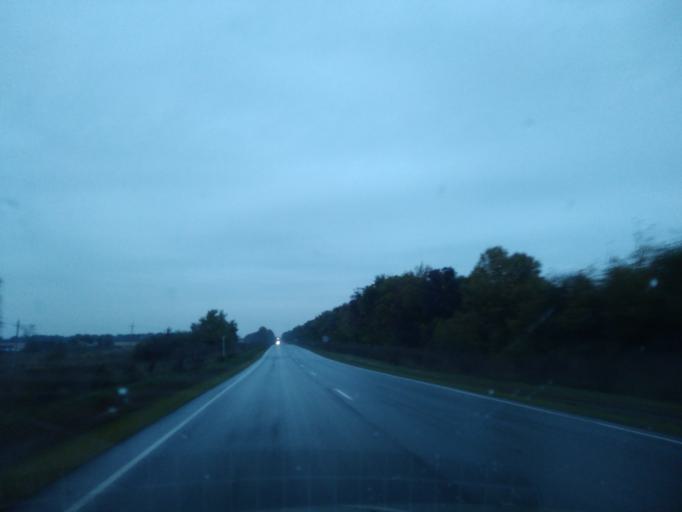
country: RU
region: Tula
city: Teploye
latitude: 53.5533
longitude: 37.6631
